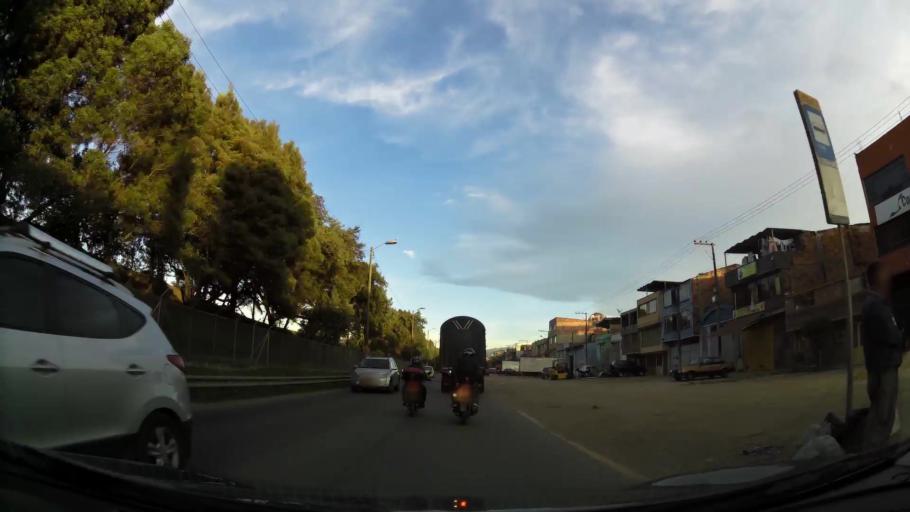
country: CO
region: Cundinamarca
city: Funza
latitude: 4.6944
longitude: -74.1506
